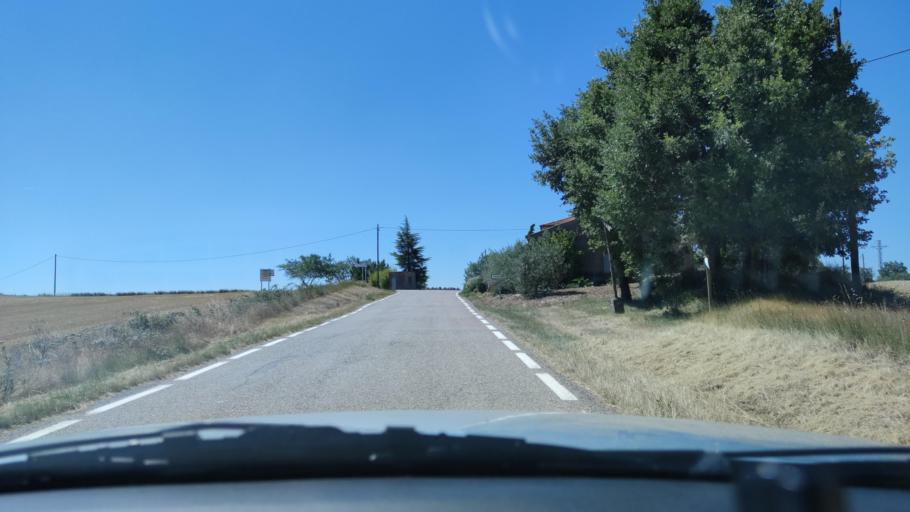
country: ES
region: Catalonia
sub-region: Provincia de Lleida
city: Solsona
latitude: 41.9206
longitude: 1.4614
